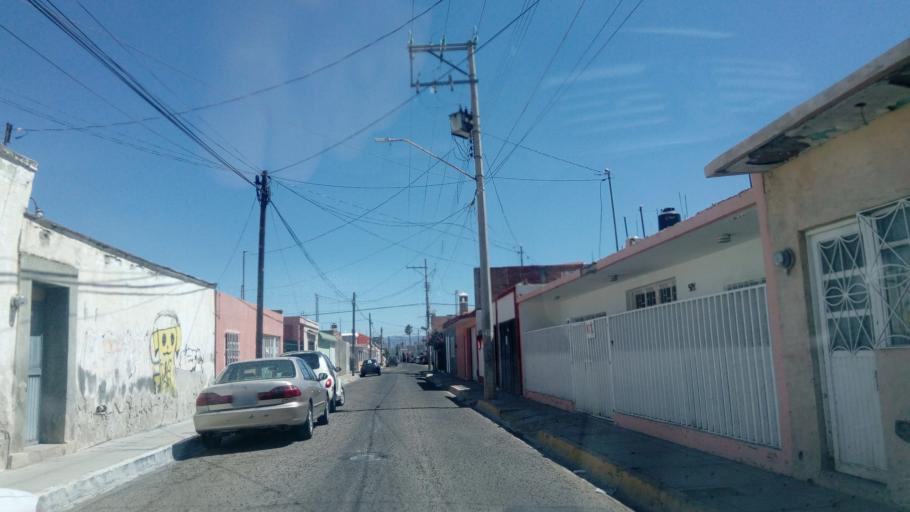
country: MX
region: Durango
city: Victoria de Durango
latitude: 24.0342
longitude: -104.6608
